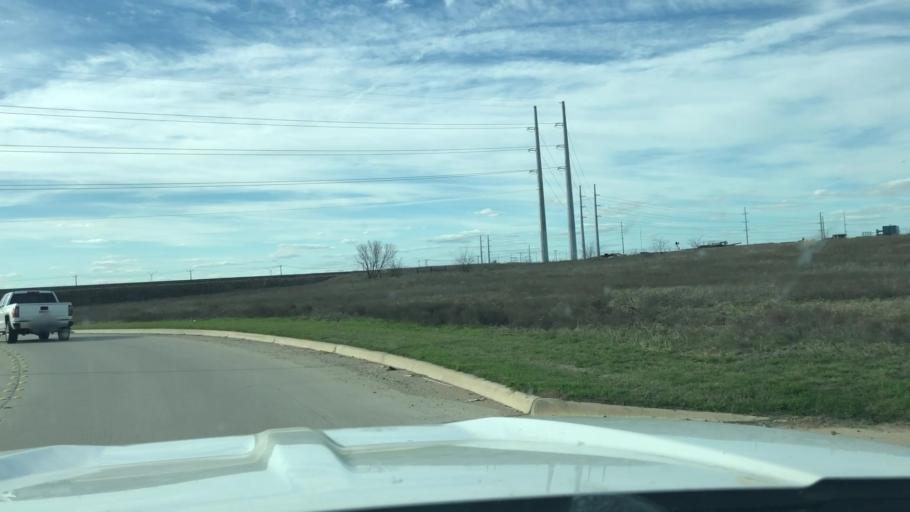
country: US
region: Texas
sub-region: Tarrant County
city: Haslet
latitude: 32.9925
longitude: -97.3564
